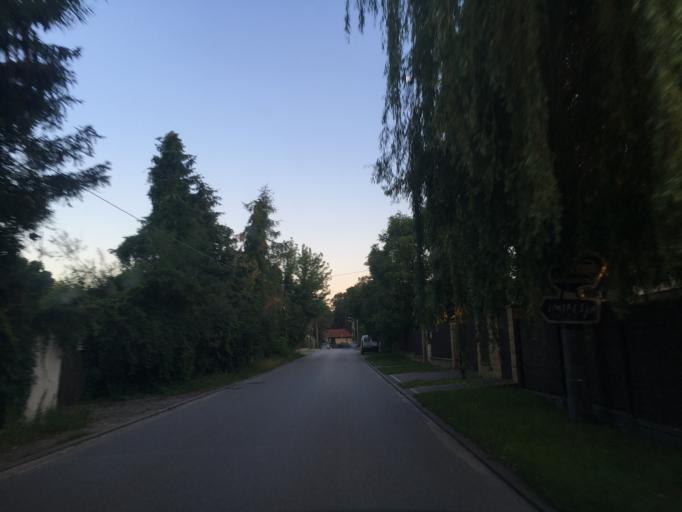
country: PL
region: Masovian Voivodeship
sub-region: Powiat piaseczynski
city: Piaseczno
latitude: 52.0659
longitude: 21.0116
